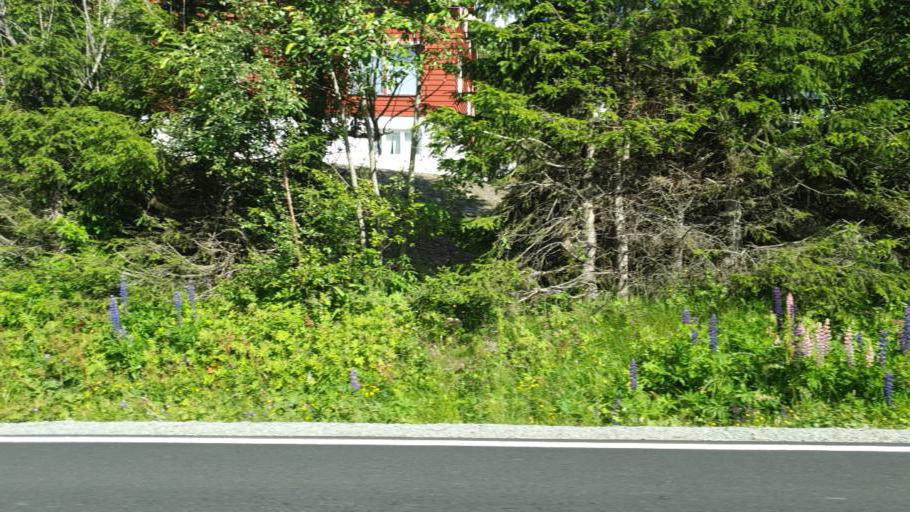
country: NO
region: Oppland
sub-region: Oystre Slidre
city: Heggenes
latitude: 61.1752
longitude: 8.9952
